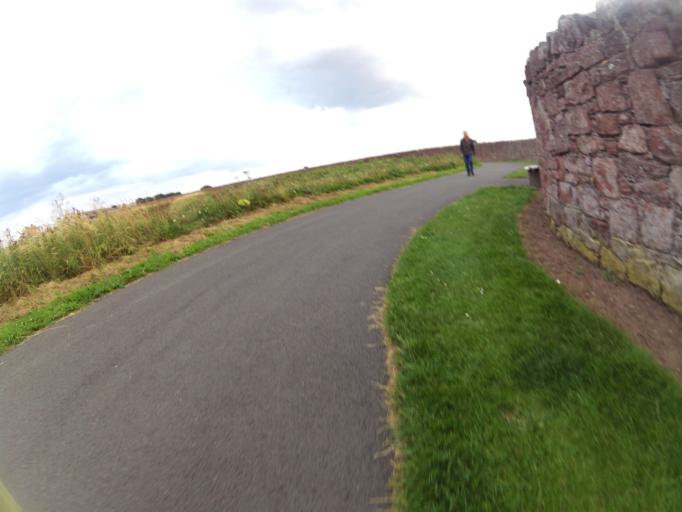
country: GB
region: Scotland
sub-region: East Lothian
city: Dunbar
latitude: 56.0062
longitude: -2.5306
